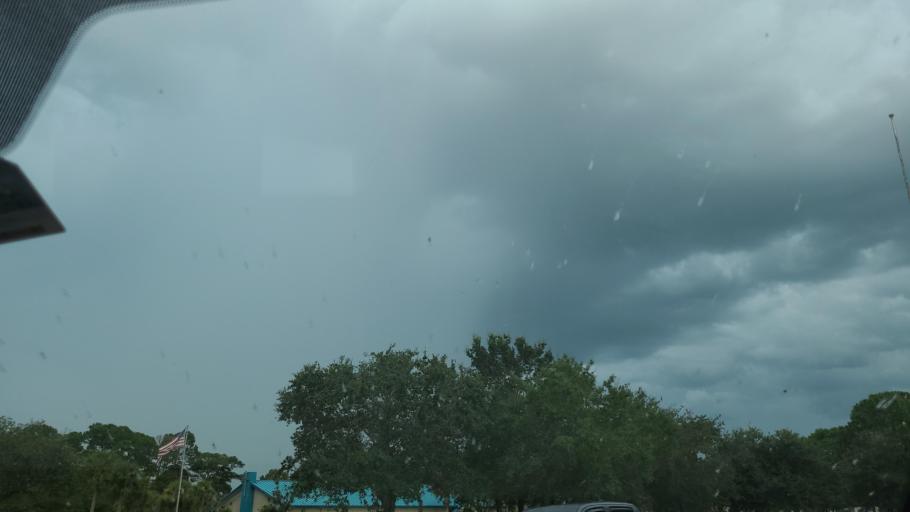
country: US
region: Florida
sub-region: Saint Lucie County
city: Port Saint Lucie
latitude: 27.2228
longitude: -80.3843
